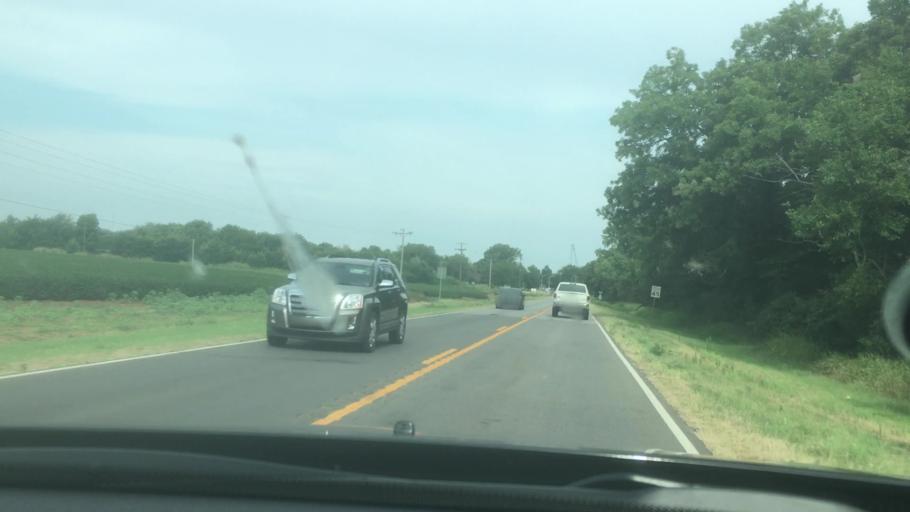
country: US
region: Oklahoma
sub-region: Garvin County
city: Maysville
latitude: 34.8161
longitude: -97.3969
